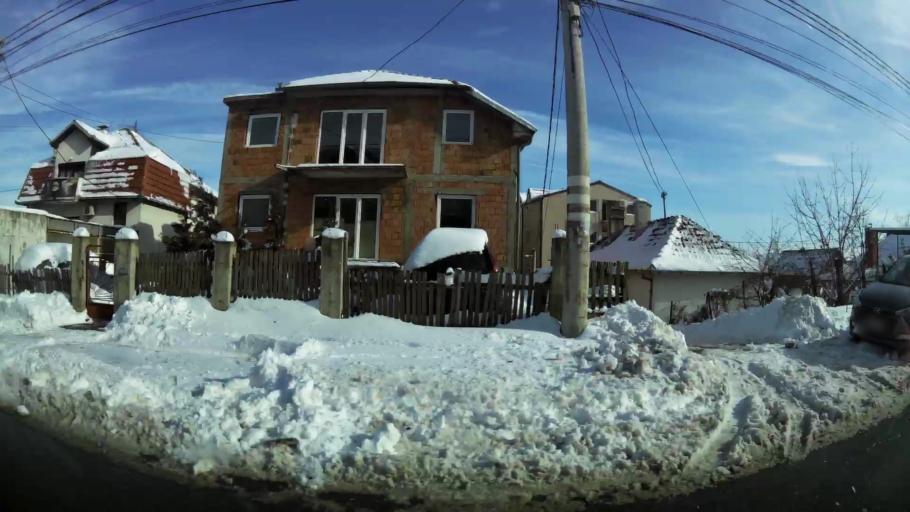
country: RS
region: Central Serbia
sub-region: Belgrade
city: Palilula
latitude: 44.8032
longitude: 20.5189
